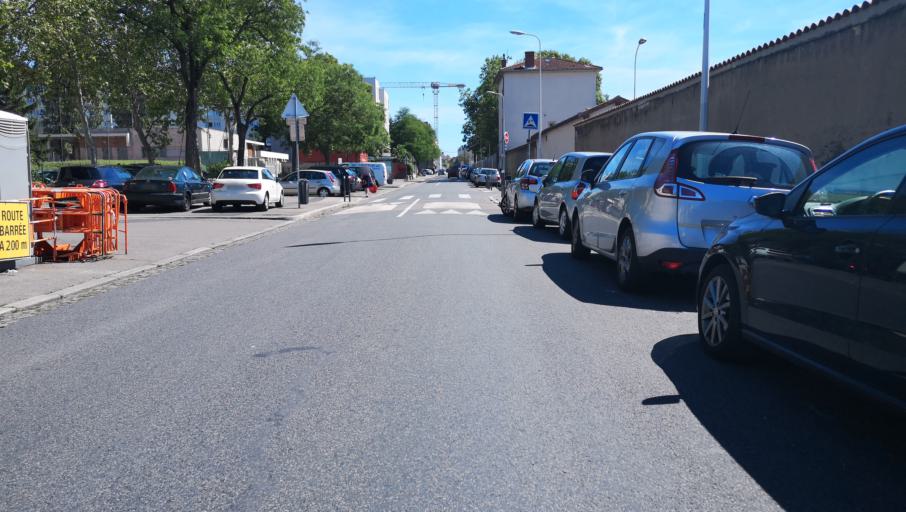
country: FR
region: Rhone-Alpes
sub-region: Departement du Rhone
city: Caluire-et-Cuire
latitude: 45.7839
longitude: 4.8209
